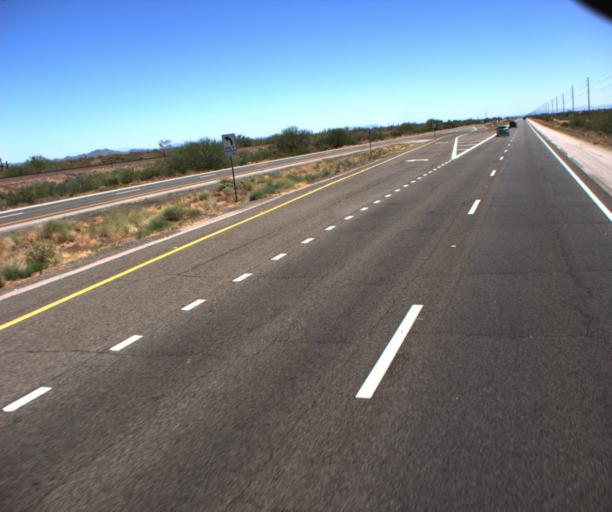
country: US
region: Arizona
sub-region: Maricopa County
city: Wickenburg
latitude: 33.8075
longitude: -112.5669
